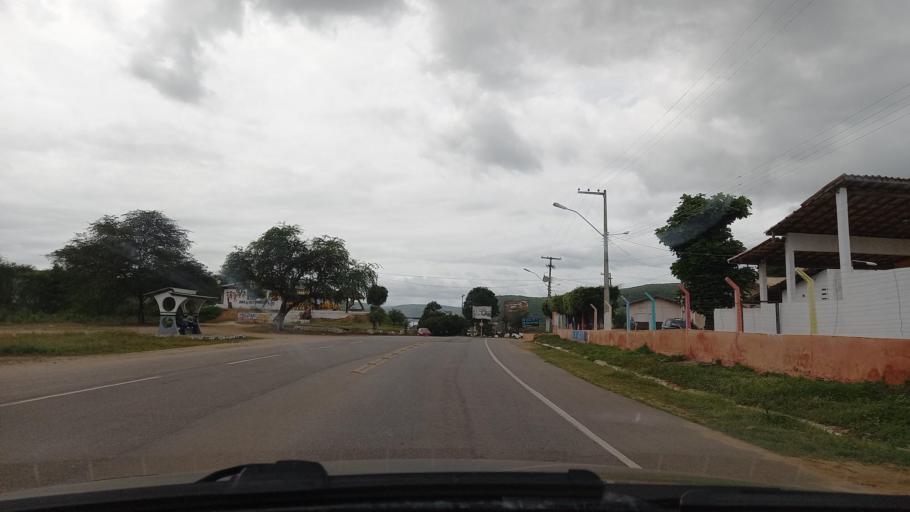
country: BR
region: Sergipe
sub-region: Caninde De Sao Francisco
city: Caninde de Sao Francisco
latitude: -9.6415
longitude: -37.7891
